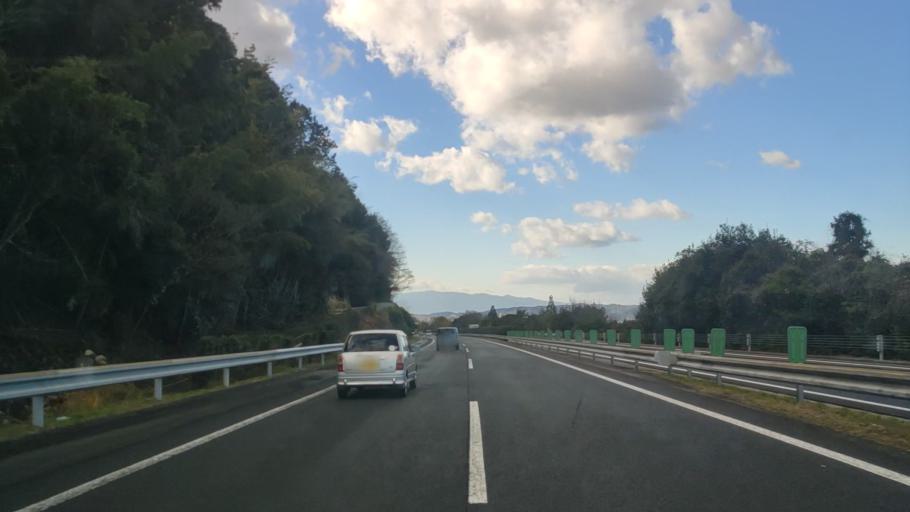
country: JP
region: Ehime
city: Niihama
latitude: 33.9291
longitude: 133.3386
